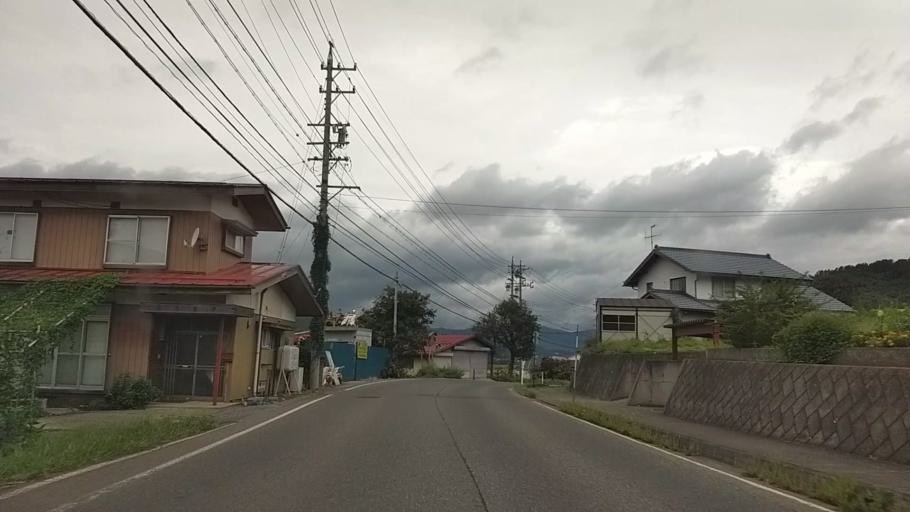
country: JP
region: Nagano
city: Iiyama
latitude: 36.8140
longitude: 138.3600
